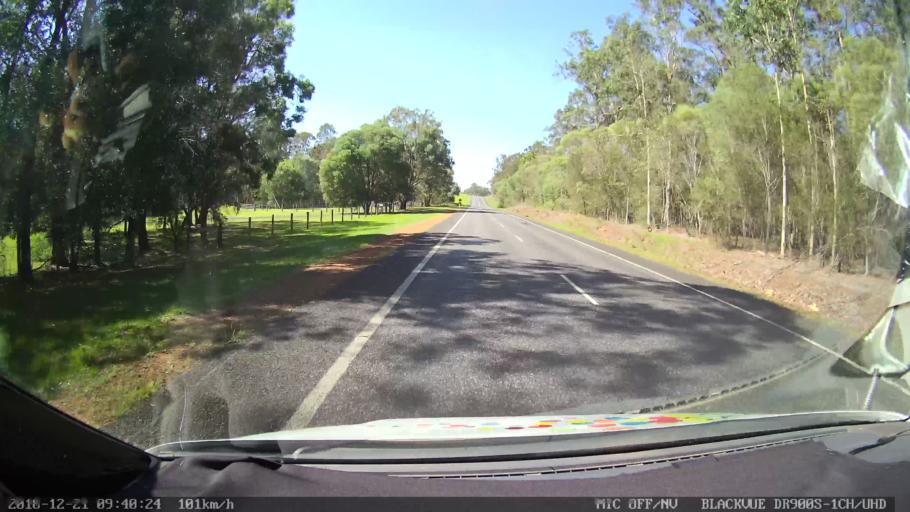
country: AU
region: New South Wales
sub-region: Clarence Valley
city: Grafton
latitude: -29.5721
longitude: 152.9636
